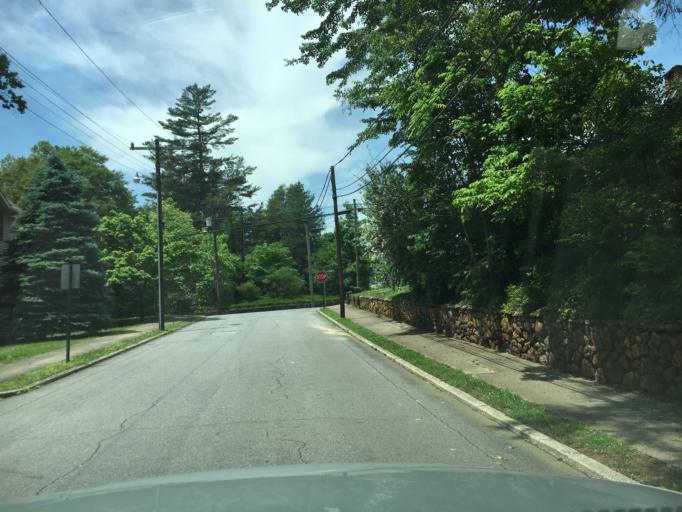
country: US
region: North Carolina
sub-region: Transylvania County
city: Brevard
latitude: 35.2296
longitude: -82.7279
